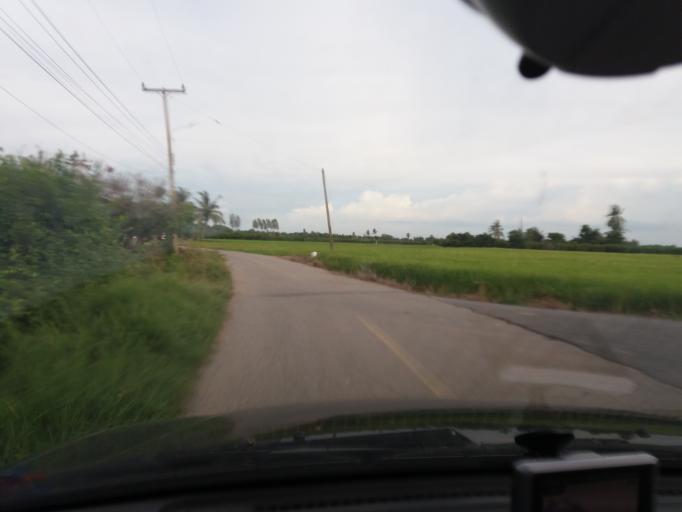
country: TH
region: Suphan Buri
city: Doembang Nangbuat
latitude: 14.8122
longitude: 100.1395
